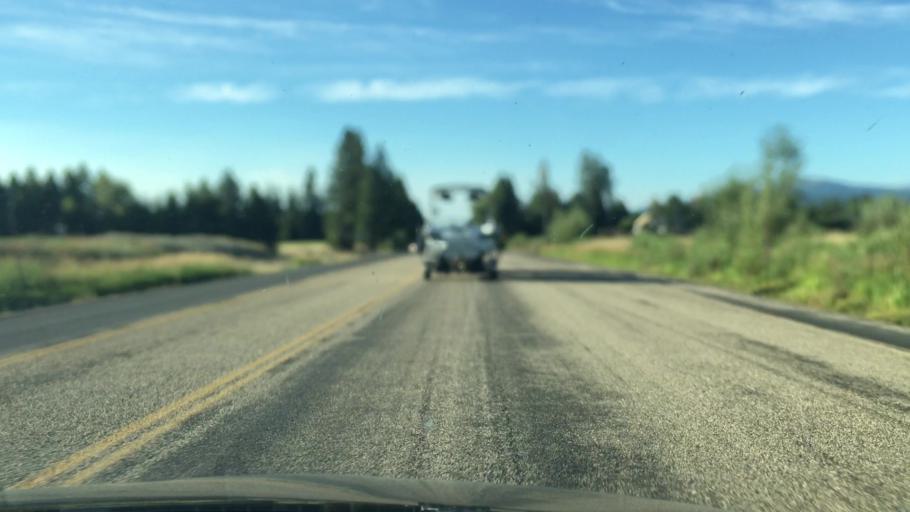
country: US
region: Idaho
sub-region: Valley County
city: Cascade
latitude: 44.6861
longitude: -116.0516
